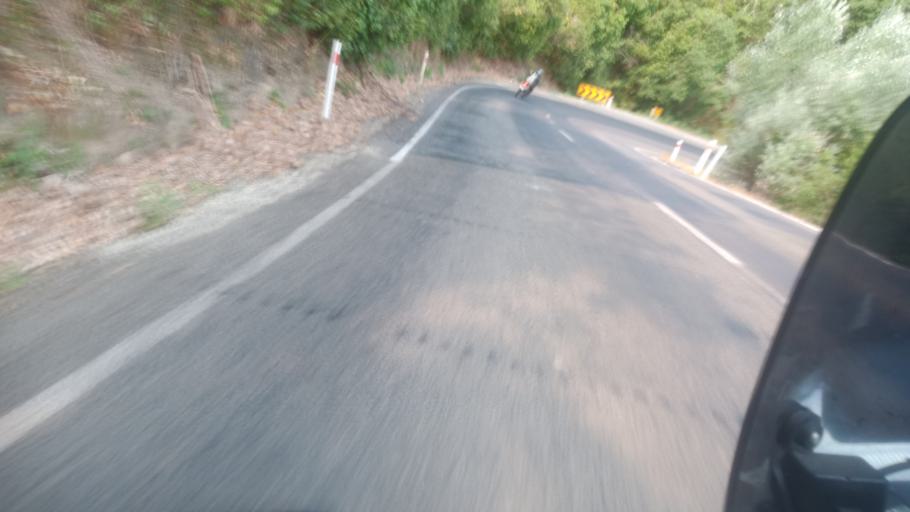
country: NZ
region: Bay of Plenty
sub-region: Opotiki District
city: Opotiki
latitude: -37.9018
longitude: 177.5505
